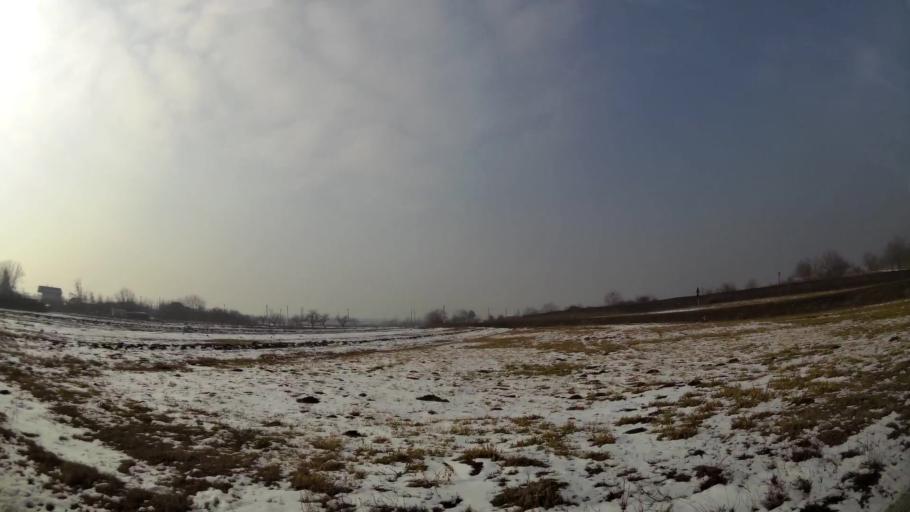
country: MK
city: Kadino
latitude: 41.9724
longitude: 21.6066
